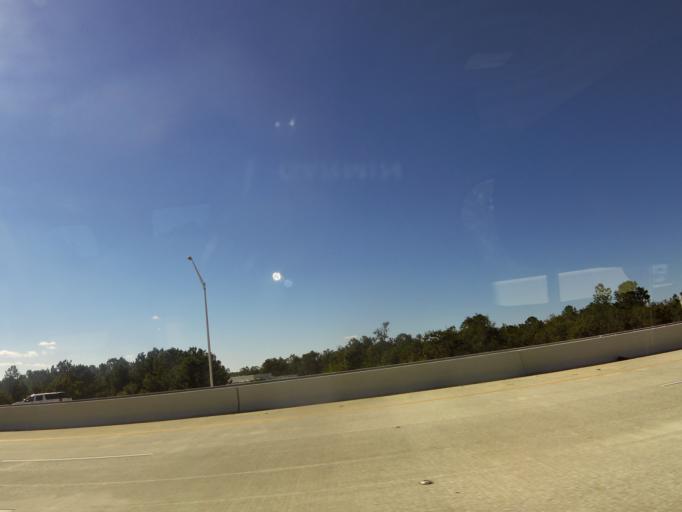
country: US
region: Florida
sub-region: Saint Johns County
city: Palm Valley
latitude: 30.1327
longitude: -81.5097
